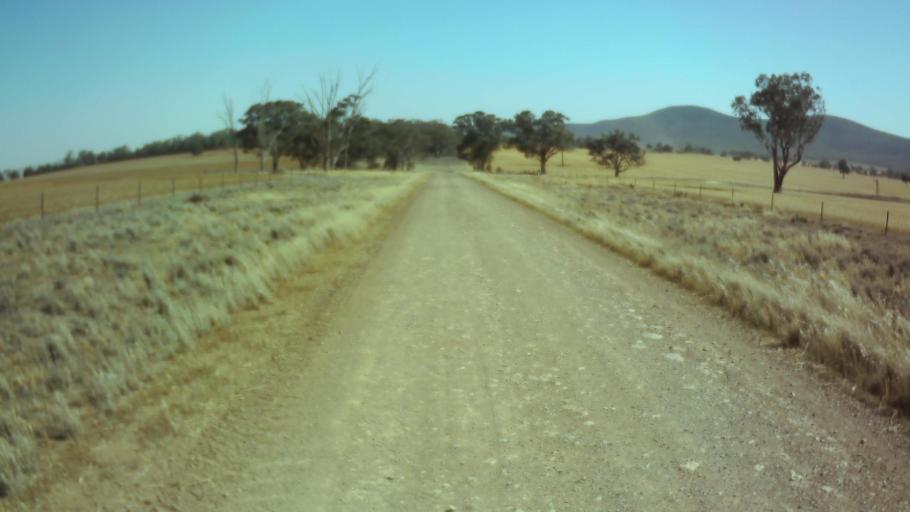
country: AU
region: New South Wales
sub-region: Weddin
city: Grenfell
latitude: -33.8533
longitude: 148.0160
